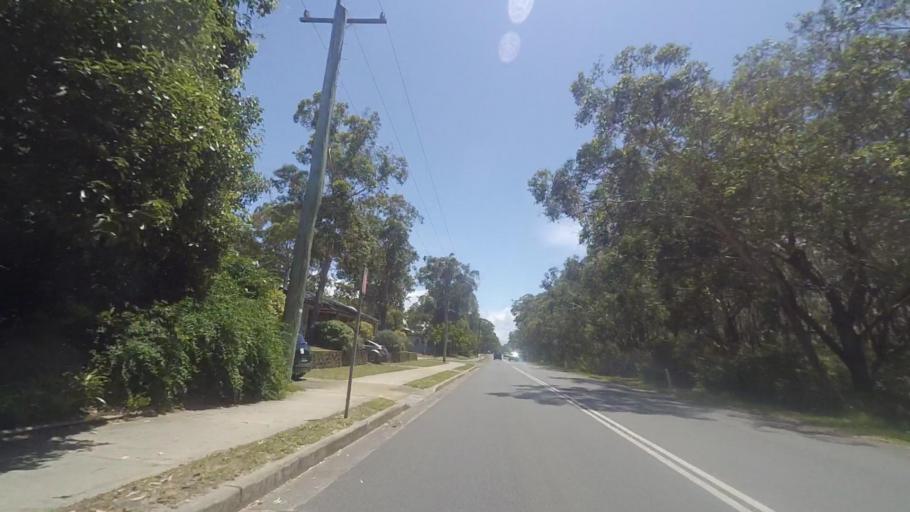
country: AU
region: New South Wales
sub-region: Great Lakes
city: Hawks Nest
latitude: -32.6702
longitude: 152.1778
